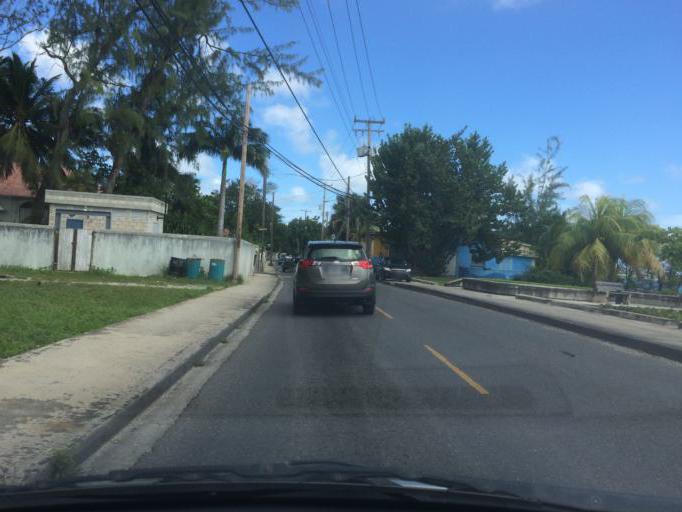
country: BB
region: Christ Church
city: Oistins
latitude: 13.0651
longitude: -59.5488
